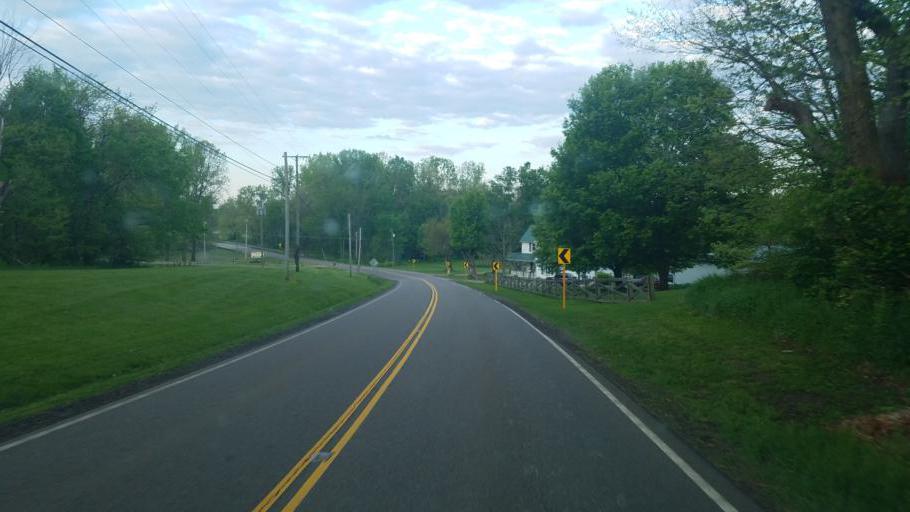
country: US
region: Ohio
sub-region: Knox County
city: Fredericktown
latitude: 40.4947
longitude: -82.5424
